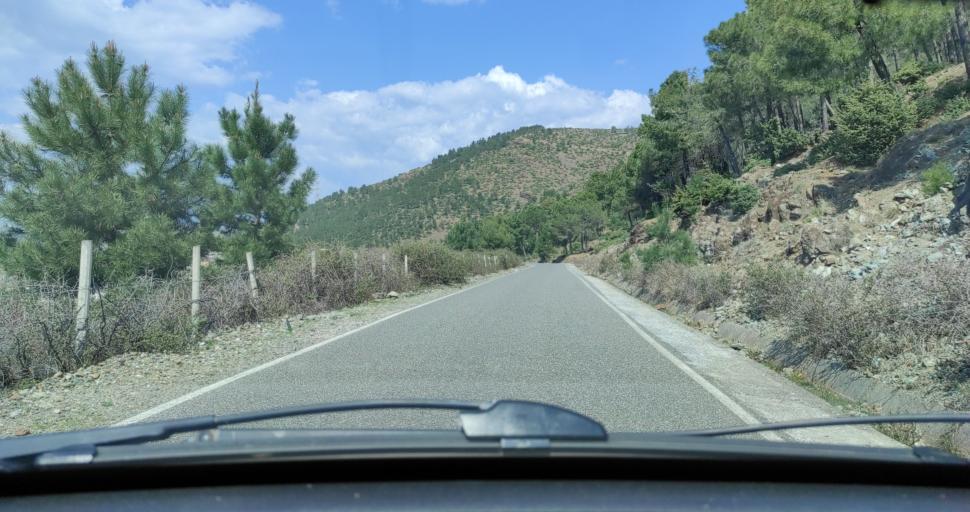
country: AL
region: Shkoder
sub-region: Rrethi i Shkodres
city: Vau i Dejes
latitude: 41.9960
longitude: 19.6492
